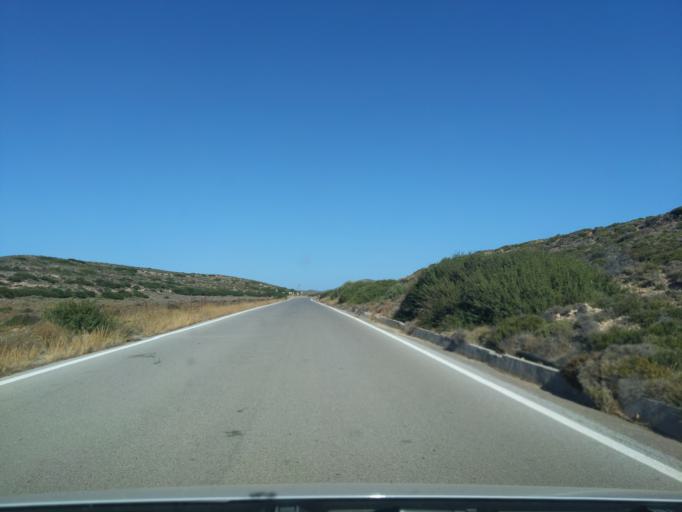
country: GR
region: Crete
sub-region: Nomos Lasithiou
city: Palekastro
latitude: 35.2364
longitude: 26.2505
